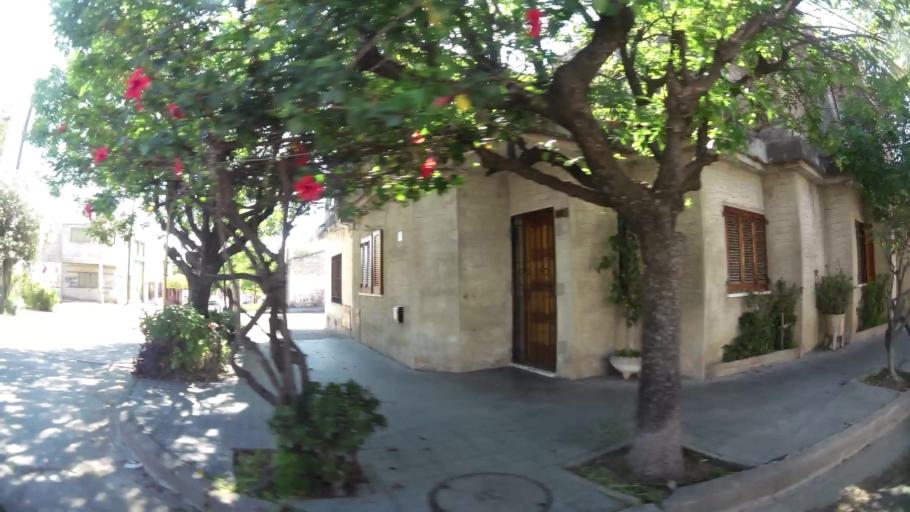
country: AR
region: Cordoba
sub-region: Departamento de Capital
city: Cordoba
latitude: -31.4110
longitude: -64.1481
